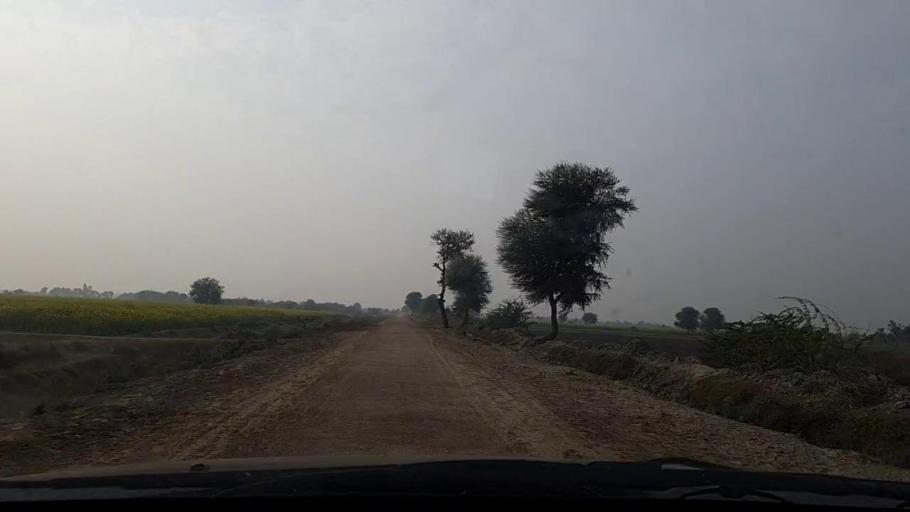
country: PK
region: Sindh
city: Pithoro
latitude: 25.7216
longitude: 69.3955
